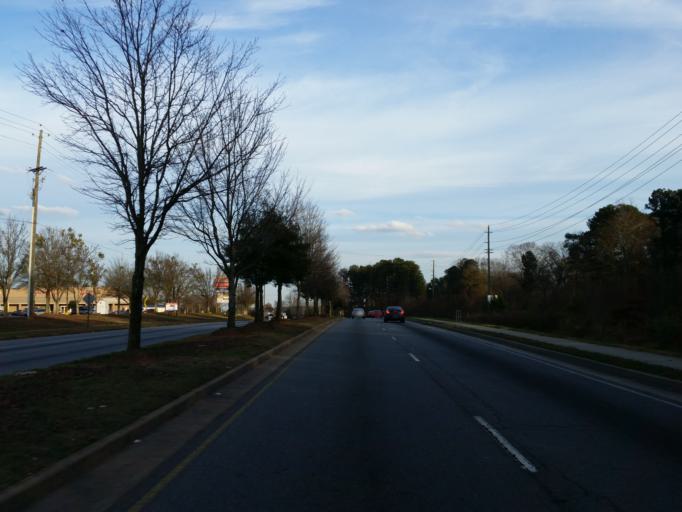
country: US
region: Georgia
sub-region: Cobb County
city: Mableton
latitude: 33.8552
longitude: -84.5959
